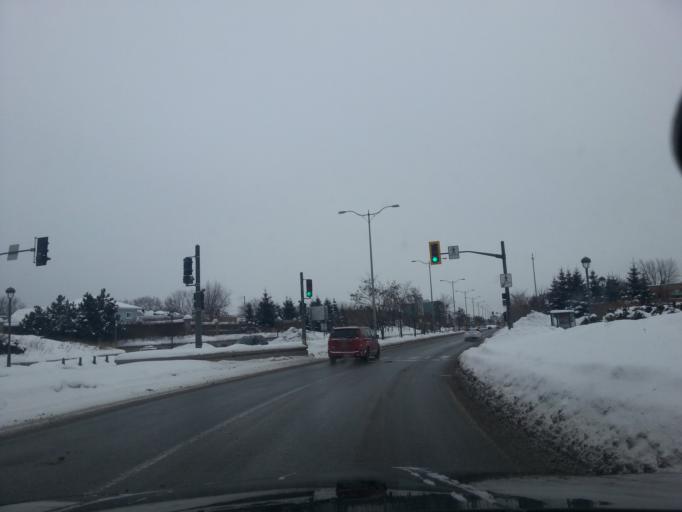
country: CA
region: Ontario
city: Ottawa
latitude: 45.4322
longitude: -75.7413
